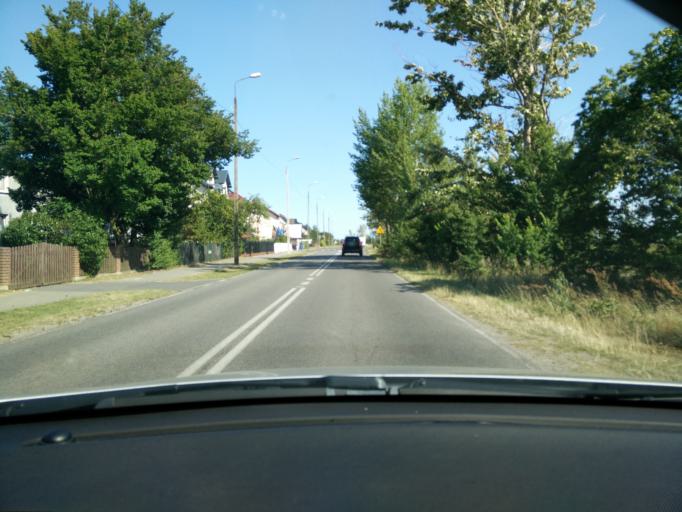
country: PL
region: Pomeranian Voivodeship
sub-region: Powiat pucki
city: Jastarnia
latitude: 54.7290
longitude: 18.5951
